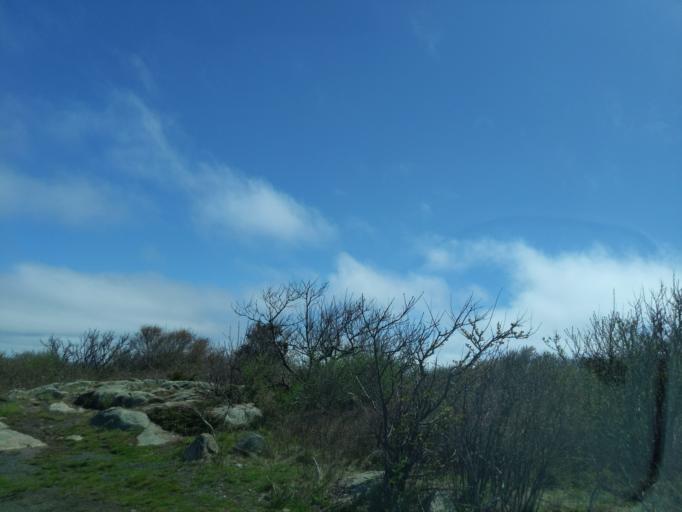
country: US
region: Massachusetts
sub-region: Essex County
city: Rockport
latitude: 42.6403
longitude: -70.5927
